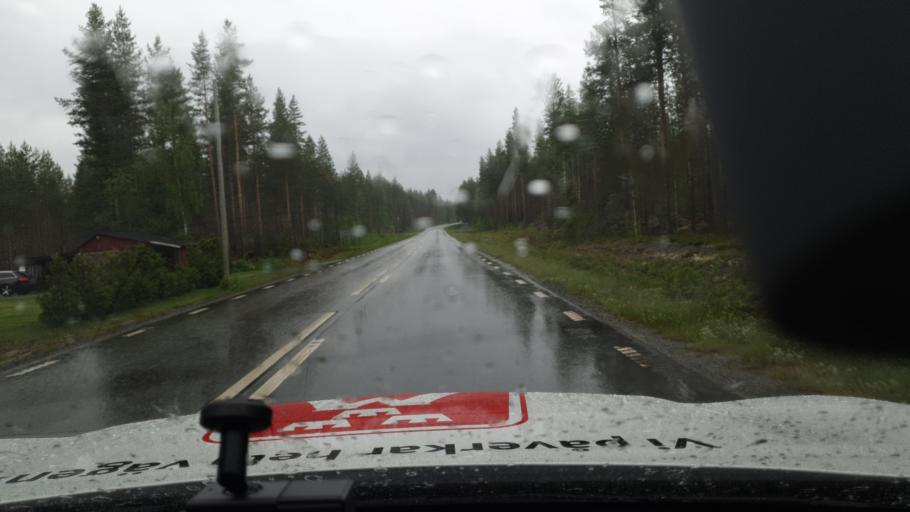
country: SE
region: Vaesterbotten
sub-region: Lycksele Kommun
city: Lycksele
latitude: 64.5305
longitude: 18.7694
